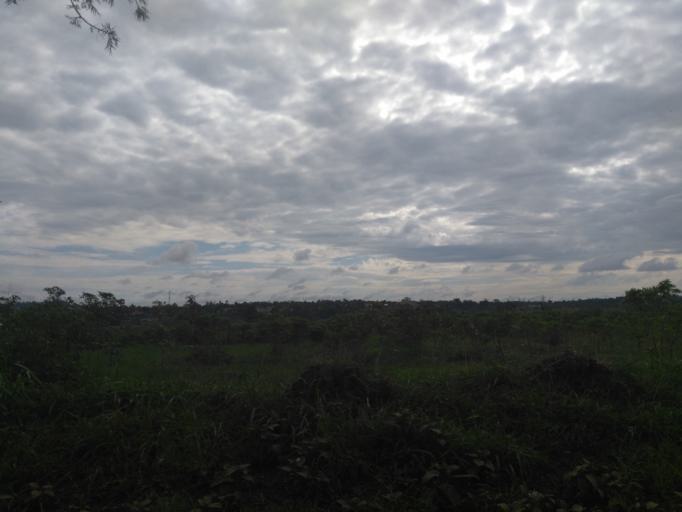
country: UG
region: Eastern Region
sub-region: Jinja District
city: Jinja
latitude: 0.4334
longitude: 33.1851
